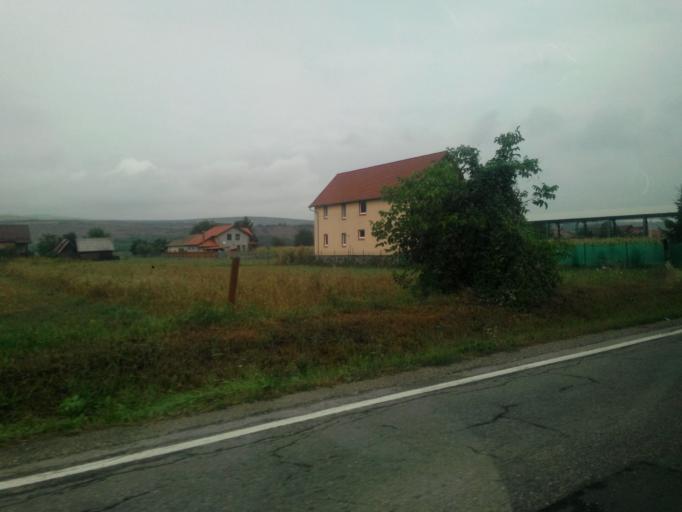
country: RO
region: Cluj
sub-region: Comuna Mihai Viteazu
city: Mihai Viteazu
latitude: 46.5355
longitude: 23.7227
